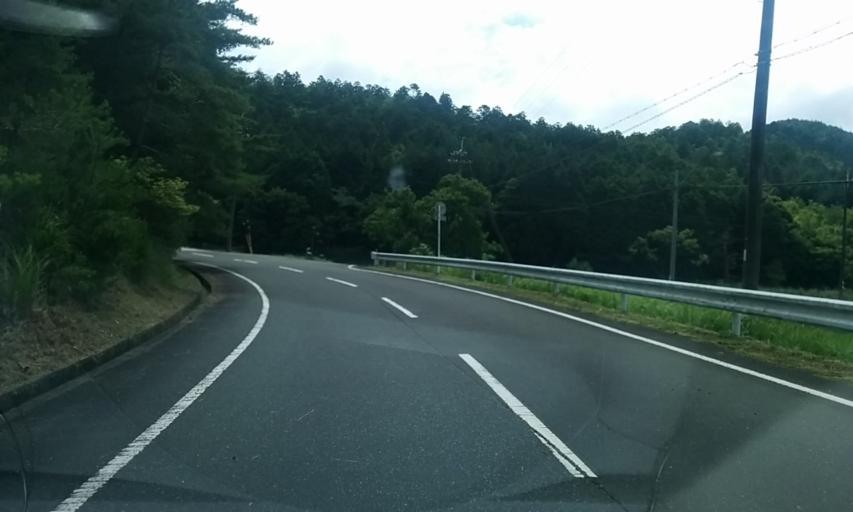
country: JP
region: Kyoto
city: Kameoka
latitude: 35.0827
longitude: 135.4857
